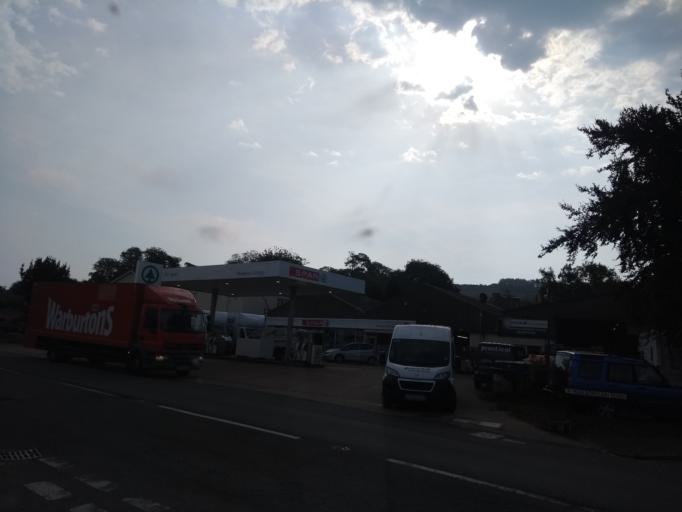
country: GB
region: England
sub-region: Devon
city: Colyton
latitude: 50.7471
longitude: -3.0329
